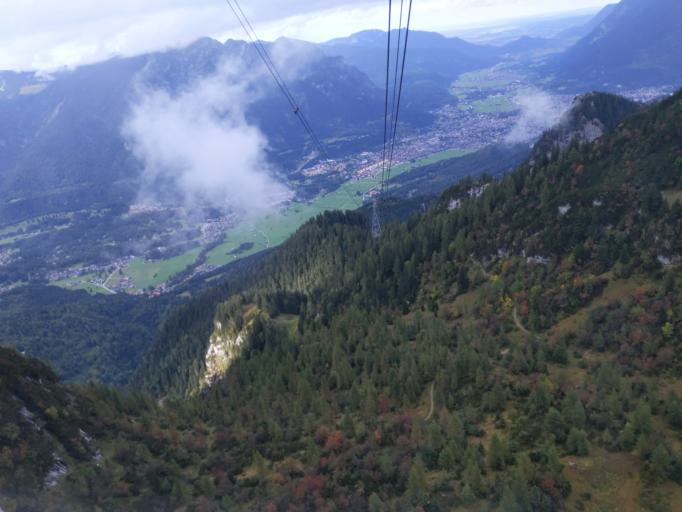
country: DE
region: Bavaria
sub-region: Upper Bavaria
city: Grainau
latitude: 47.4432
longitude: 11.0524
